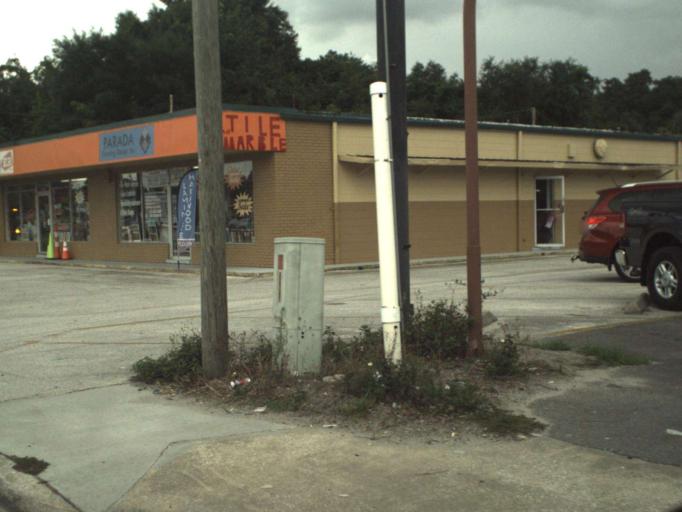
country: US
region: Florida
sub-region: Seminole County
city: Fern Park
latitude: 28.6633
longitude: -81.3484
